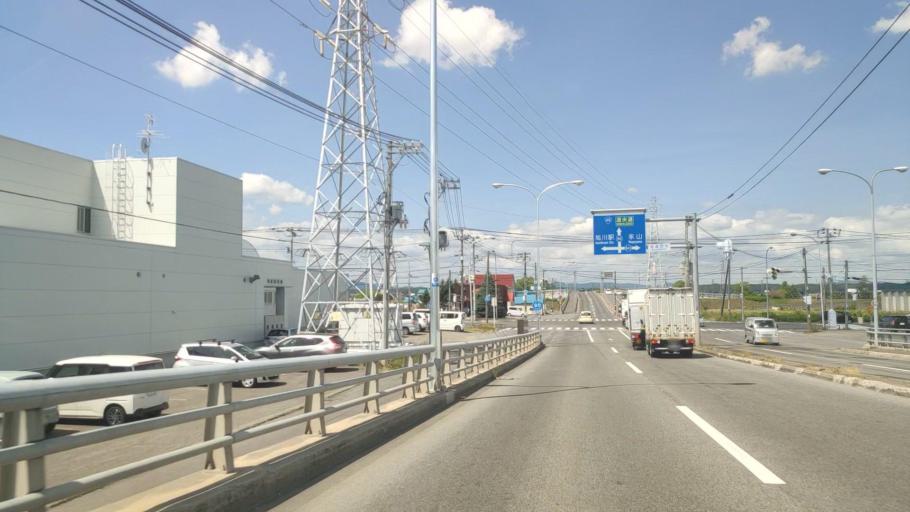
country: JP
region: Hokkaido
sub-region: Asahikawa-shi
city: Asahikawa
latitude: 43.7948
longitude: 142.3996
